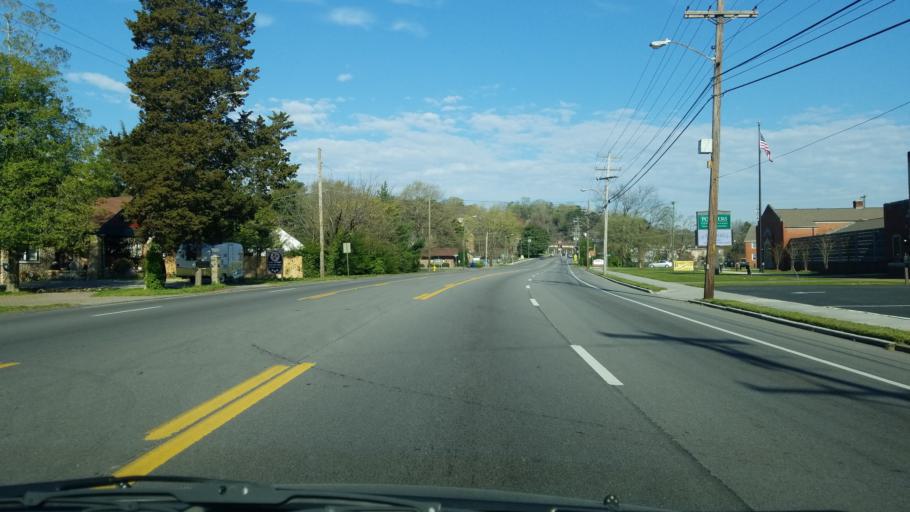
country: US
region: Tennessee
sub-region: Hamilton County
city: East Ridge
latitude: 35.0161
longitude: -85.2357
